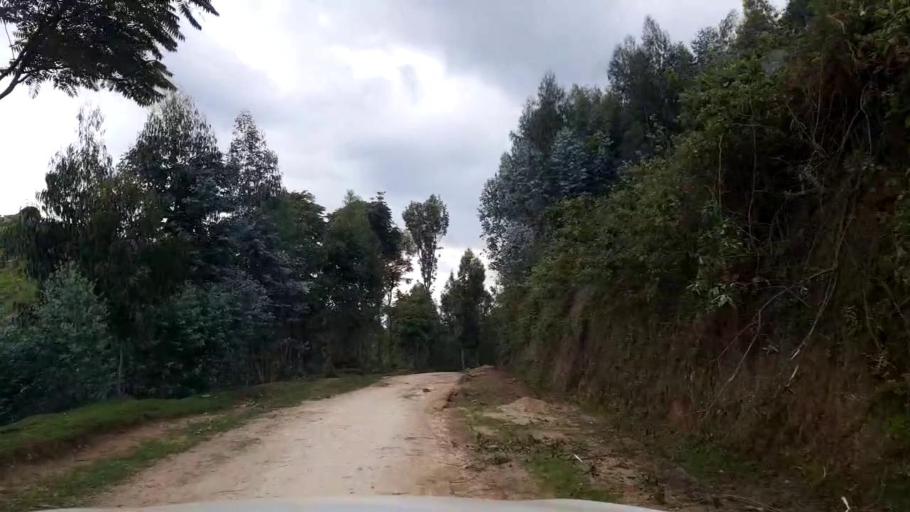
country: RW
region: Western Province
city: Kibuye
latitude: -1.8649
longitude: 29.5518
